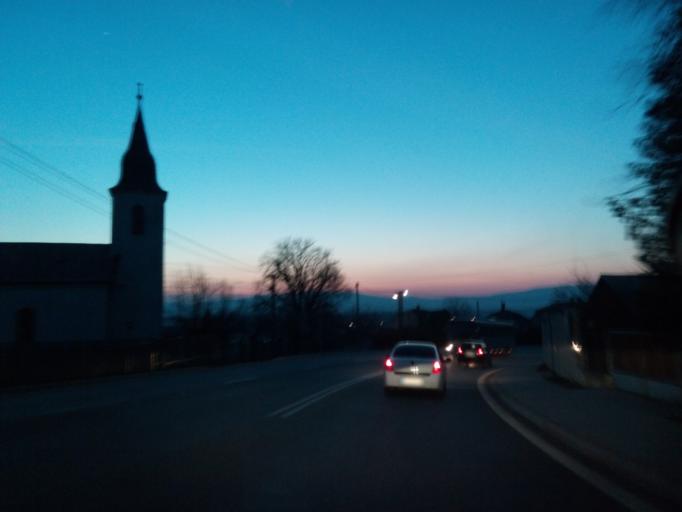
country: SK
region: Kosicky
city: Trebisov
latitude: 48.6980
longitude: 21.8081
